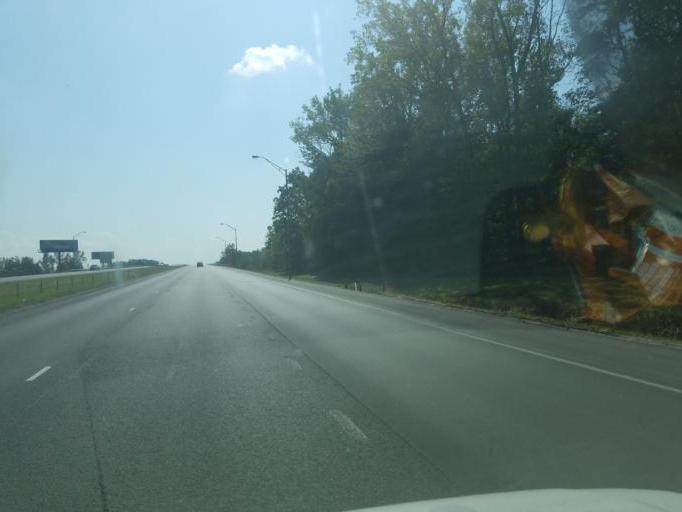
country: US
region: Indiana
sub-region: DeKalb County
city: Waterloo
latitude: 41.4368
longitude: -85.0540
